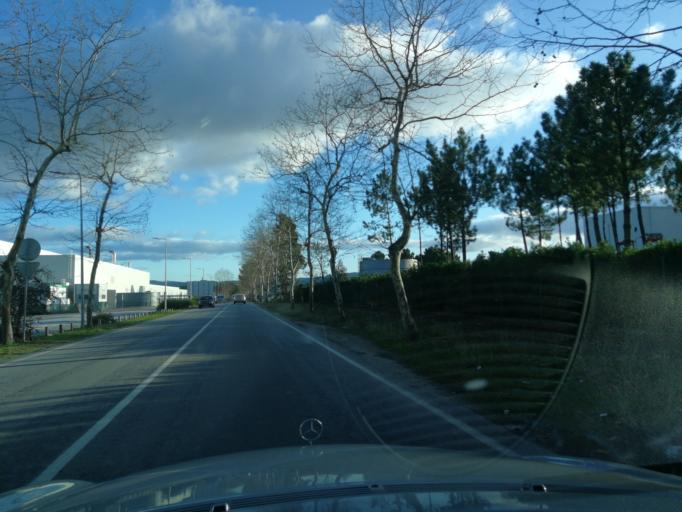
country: PT
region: Viana do Castelo
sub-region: Viana do Castelo
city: Darque
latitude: 41.6388
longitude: -8.7673
